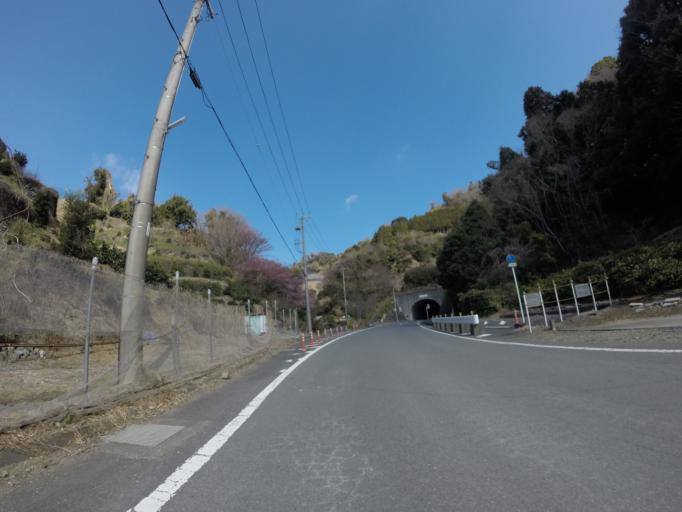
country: JP
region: Shizuoka
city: Shizuoka-shi
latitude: 35.0508
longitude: 138.4957
